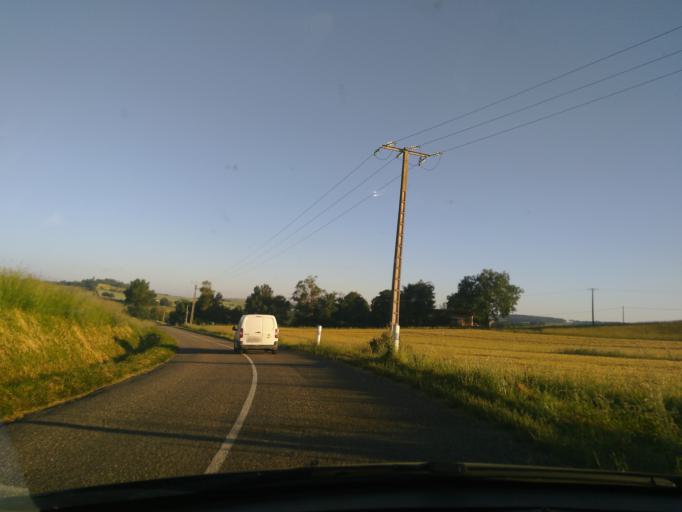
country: FR
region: Midi-Pyrenees
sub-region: Departement du Gers
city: Jegun
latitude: 43.8695
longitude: 0.4862
